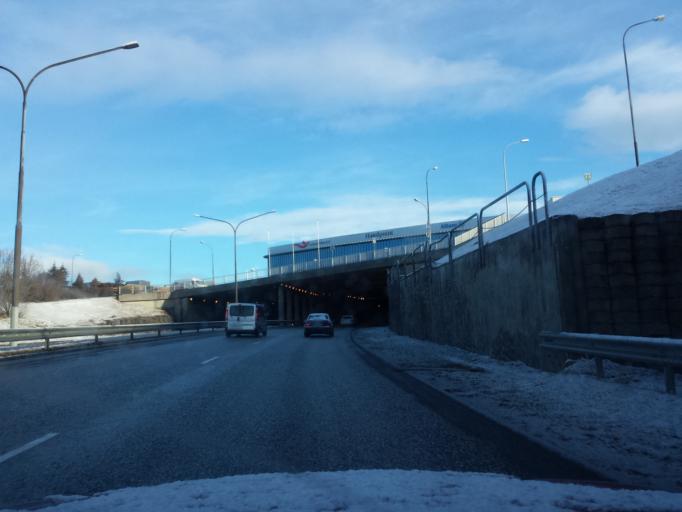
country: IS
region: Capital Region
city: Kopavogur
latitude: 64.1101
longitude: -21.9077
